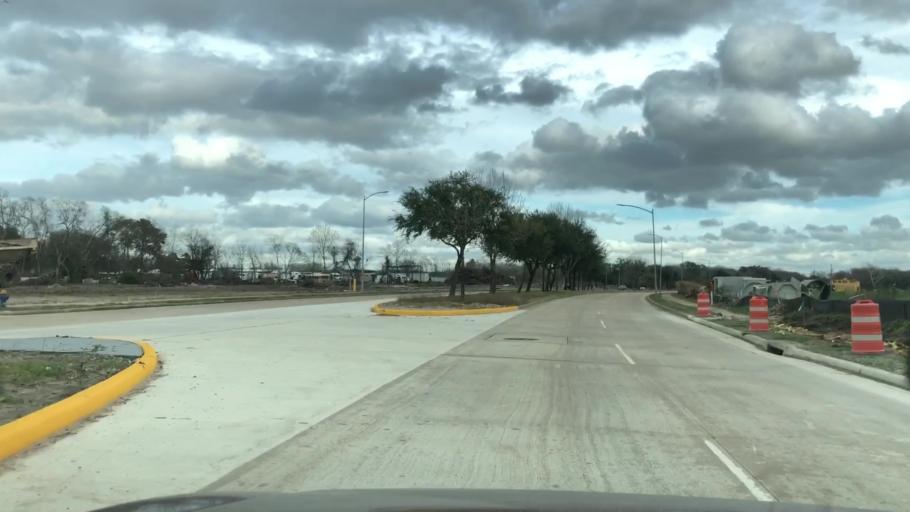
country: US
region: Texas
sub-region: Fort Bend County
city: Missouri City
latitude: 29.6115
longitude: -95.4696
